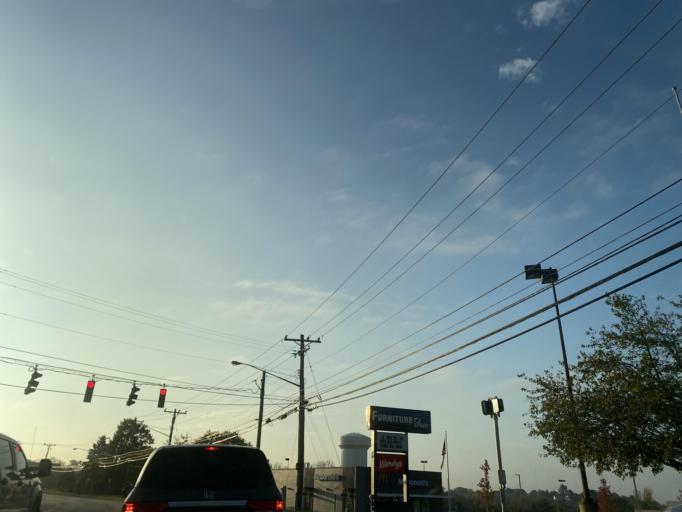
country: US
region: Kentucky
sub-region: Campbell County
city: Highland Heights
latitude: 39.0267
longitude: -84.4485
